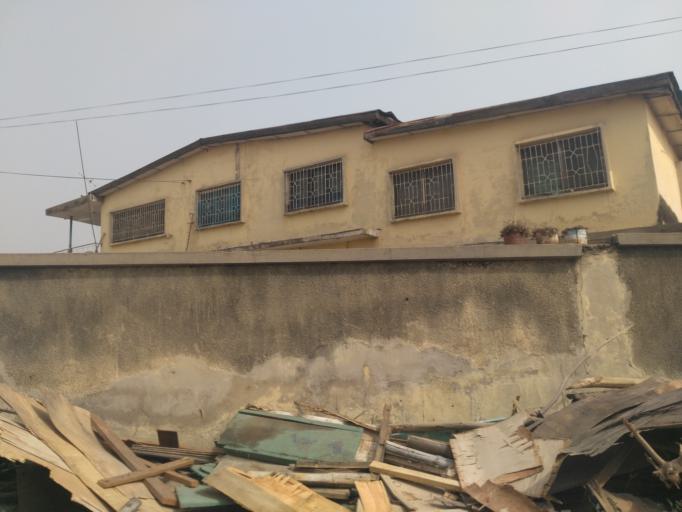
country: GH
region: Ashanti
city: Kumasi
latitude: 6.6746
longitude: -1.6028
